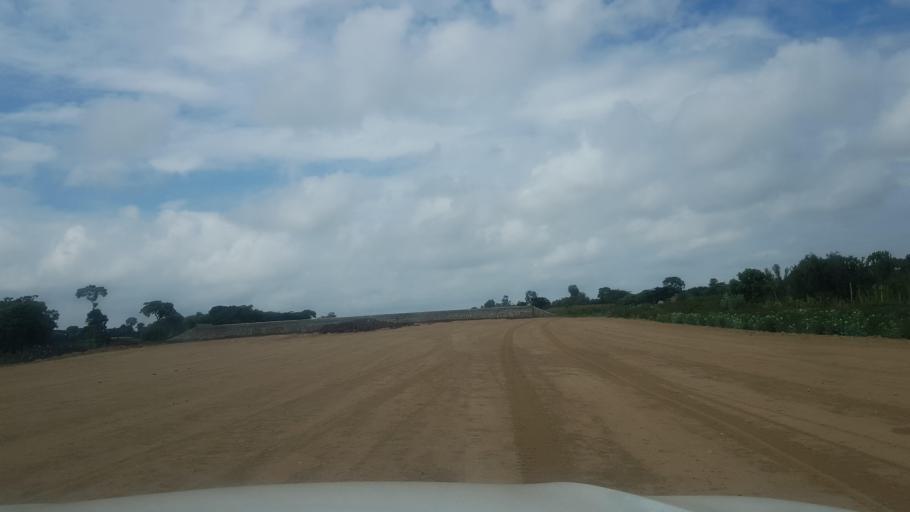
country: ET
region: Oromiya
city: Shashemene
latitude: 7.2678
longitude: 38.5979
